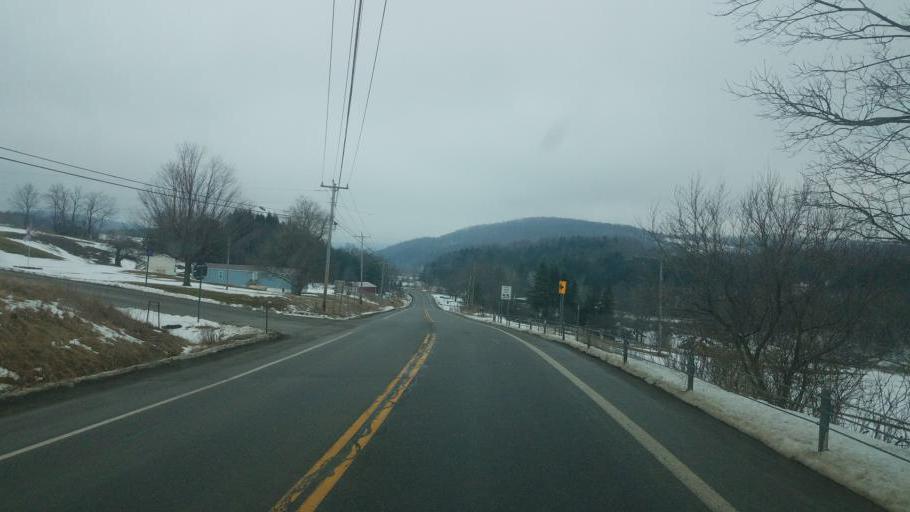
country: US
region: Pennsylvania
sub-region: Tioga County
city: Westfield
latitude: 42.0391
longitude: -77.5442
